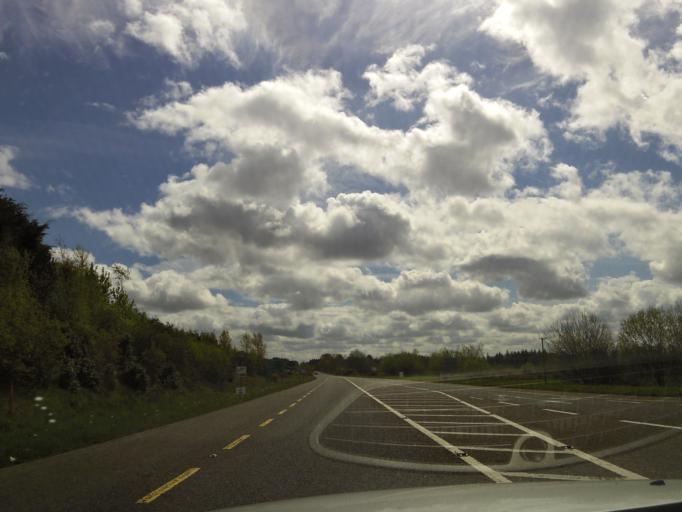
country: IE
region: Connaught
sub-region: Maigh Eo
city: Claremorris
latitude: 53.7078
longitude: -8.9837
